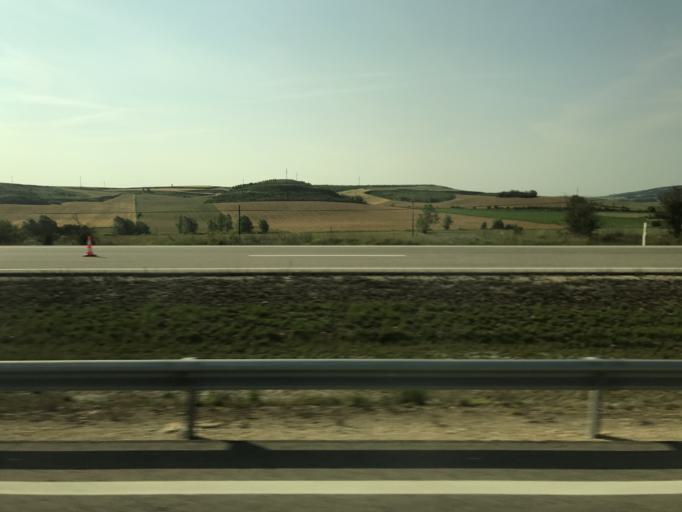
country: ES
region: Castille and Leon
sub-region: Provincia de Burgos
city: Quintanapalla
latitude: 42.4160
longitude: -3.5249
